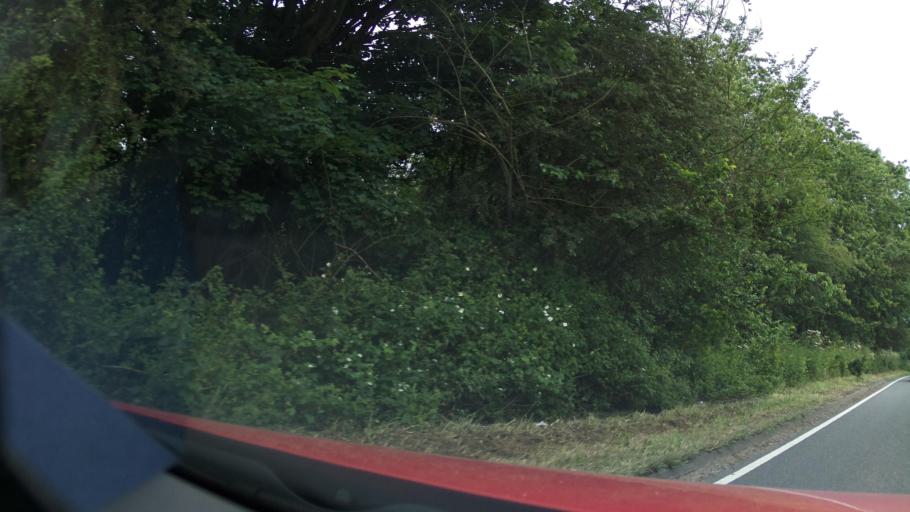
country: GB
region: England
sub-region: Leicestershire
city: Grimston
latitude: 52.7995
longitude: -1.0503
